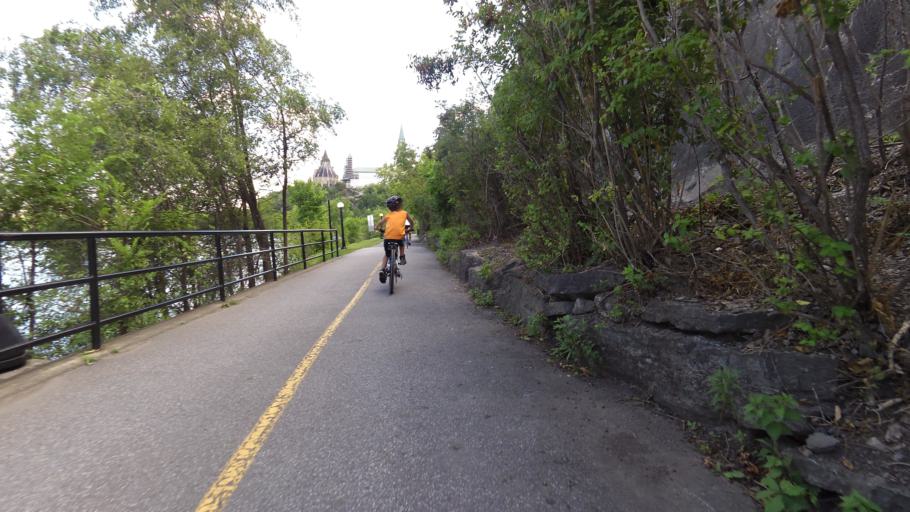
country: CA
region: Ontario
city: Ottawa
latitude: 45.4227
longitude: -75.7066
